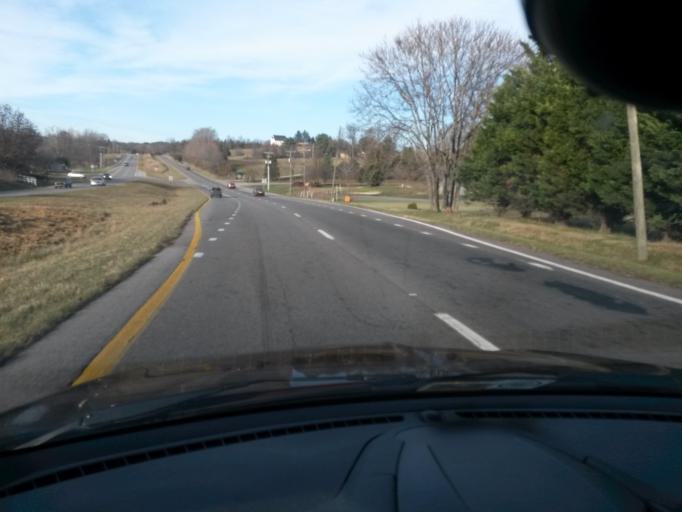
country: US
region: Virginia
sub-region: Botetourt County
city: Daleville
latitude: 37.4361
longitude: -79.9033
